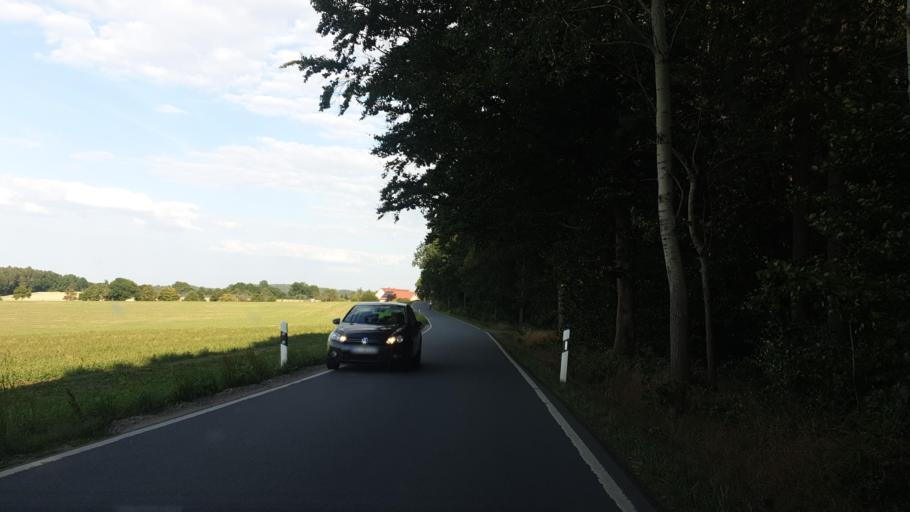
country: DE
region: Saxony
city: Lichtenstein
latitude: 50.7363
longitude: 12.6290
